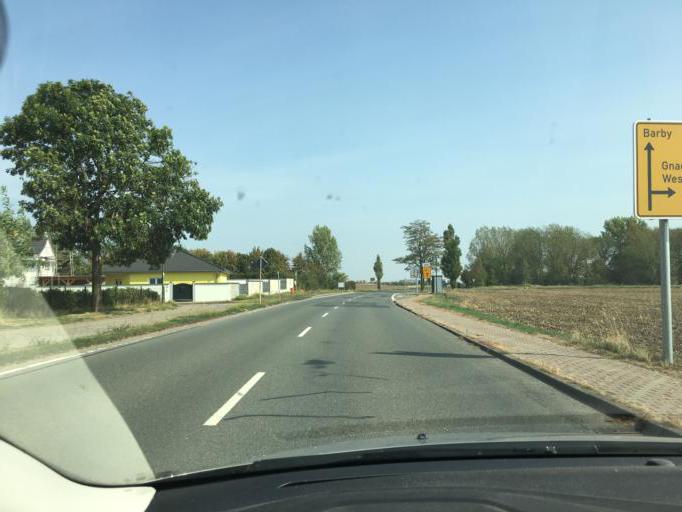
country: DE
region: Saxony-Anhalt
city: Barby
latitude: 51.9913
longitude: 11.8406
